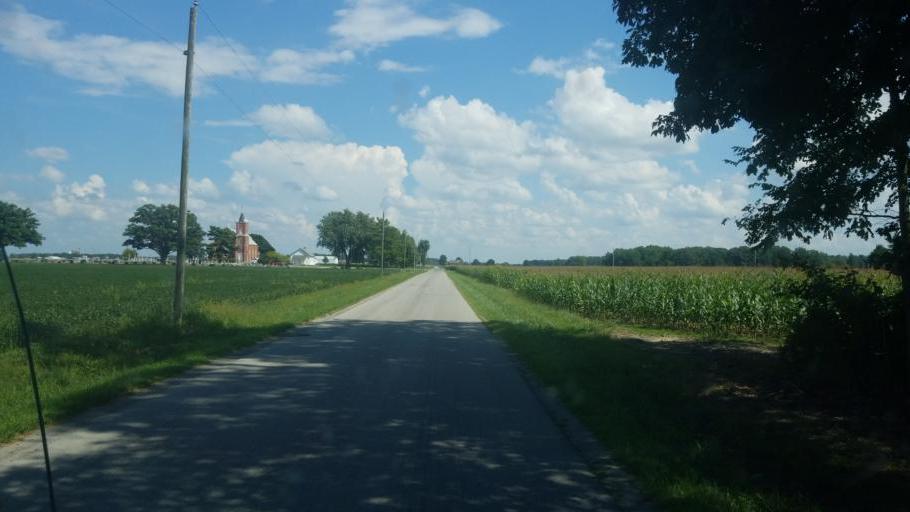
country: US
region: Ohio
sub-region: Wyandot County
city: Carey
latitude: 40.8758
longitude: -83.3604
